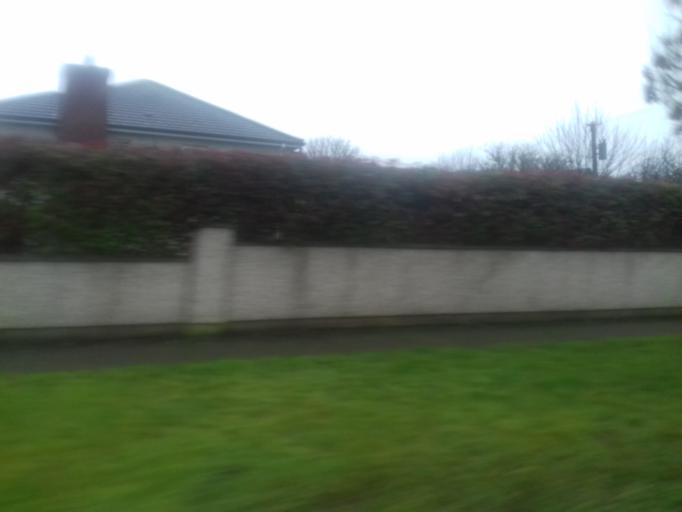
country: IE
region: Leinster
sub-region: County Carlow
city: Bagenalstown
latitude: 52.6779
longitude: -7.0221
